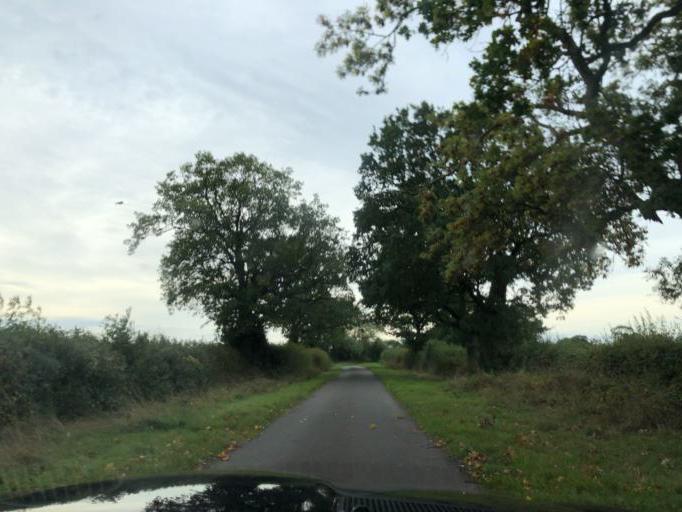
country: GB
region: England
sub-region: Warwickshire
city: Wroxall
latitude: 52.3202
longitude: -1.6558
